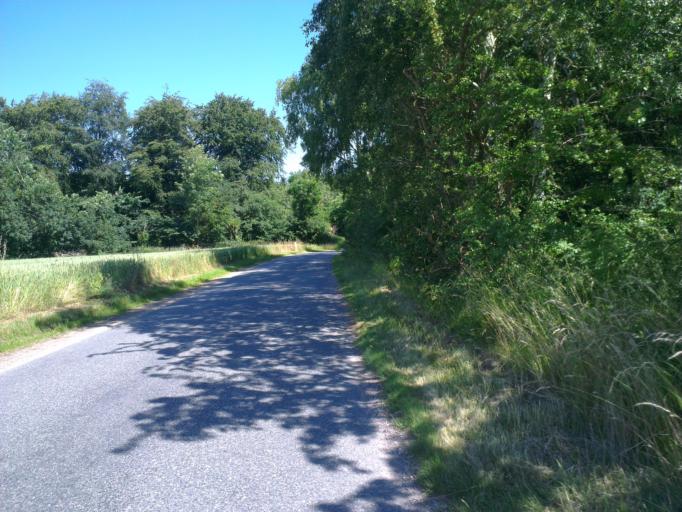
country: DK
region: Capital Region
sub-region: Frederikssund Kommune
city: Jaegerspris
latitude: 55.8136
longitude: 11.9329
